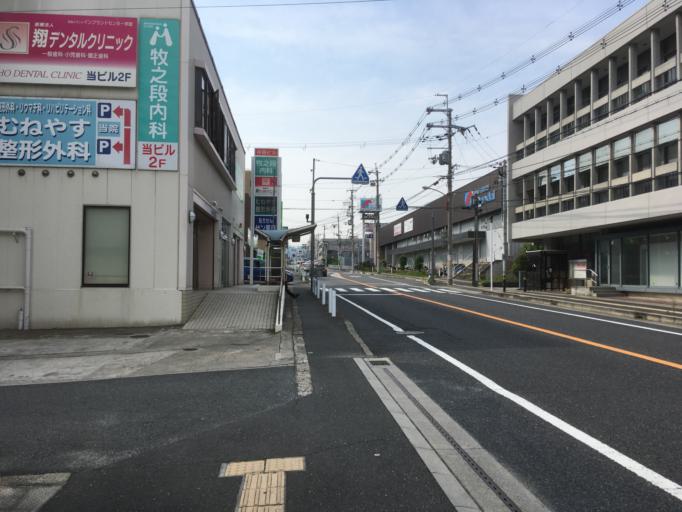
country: JP
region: Nara
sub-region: Ikoma-shi
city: Ikoma
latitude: 34.6949
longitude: 135.7018
